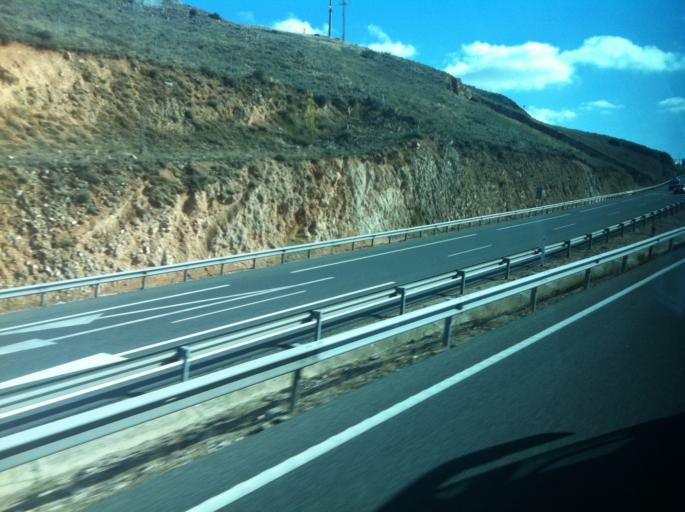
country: ES
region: Castille and Leon
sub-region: Provincia de Segovia
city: Honrubia de la Cuesta
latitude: 41.5144
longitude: -3.7170
